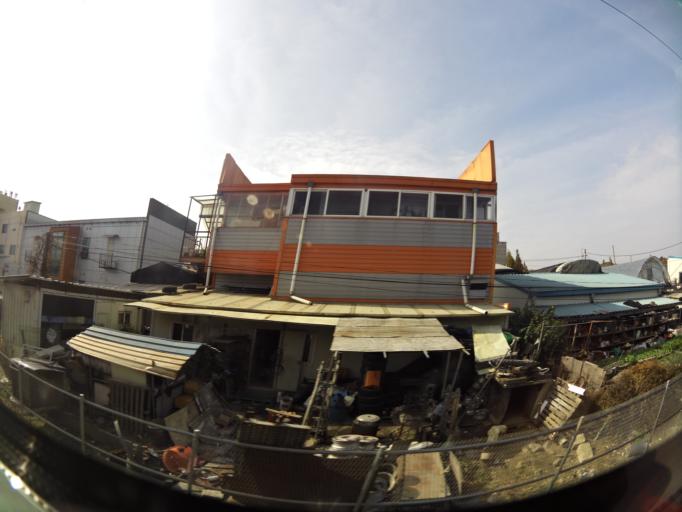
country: KR
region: Chungcheongbuk-do
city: Cheongju-si
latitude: 36.6077
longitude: 127.2943
